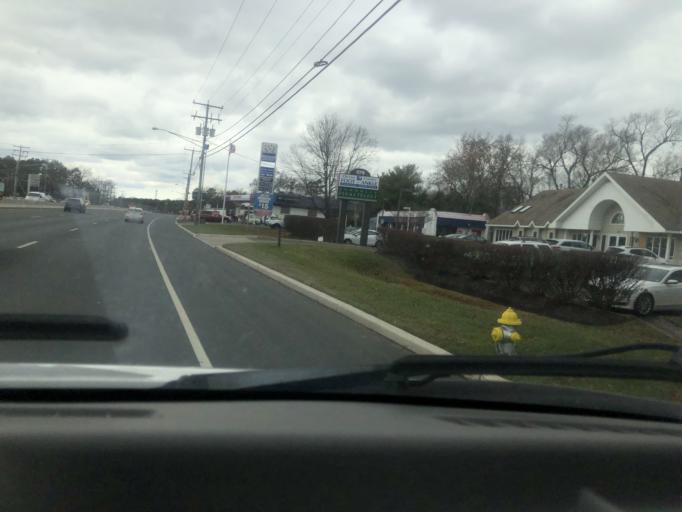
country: US
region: New Jersey
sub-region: Ocean County
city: Pine Lake Park
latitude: 39.9785
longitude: -74.2483
